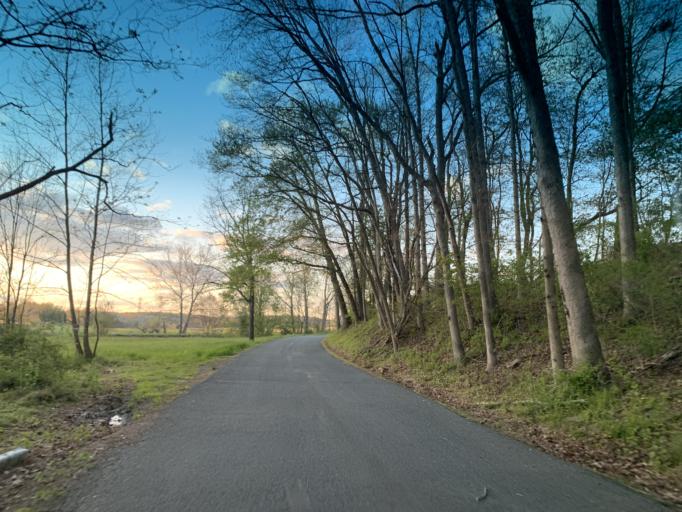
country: US
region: Maryland
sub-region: Harford County
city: Jarrettsville
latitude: 39.6532
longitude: -76.4372
